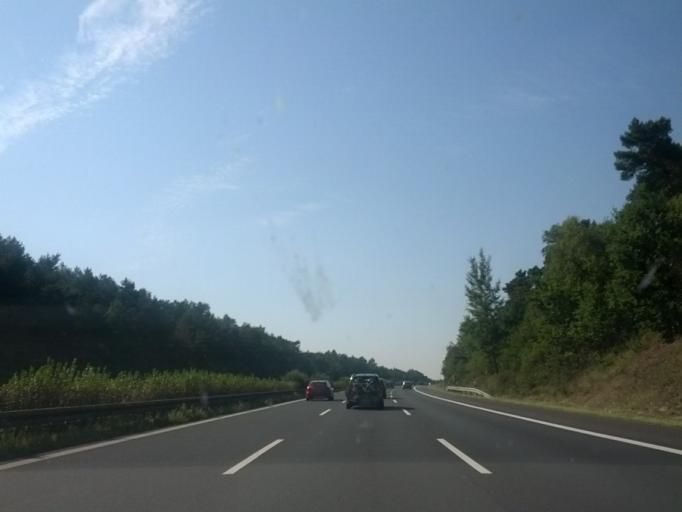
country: DE
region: Brandenburg
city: Beelitz
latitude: 52.2306
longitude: 12.9152
